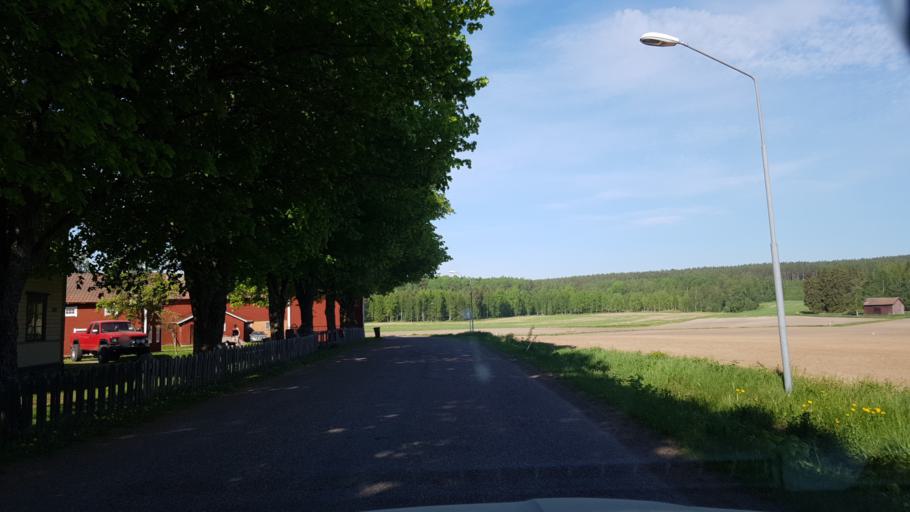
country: SE
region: Dalarna
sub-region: Hedemora Kommun
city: Langshyttan
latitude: 60.4189
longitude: 15.9392
